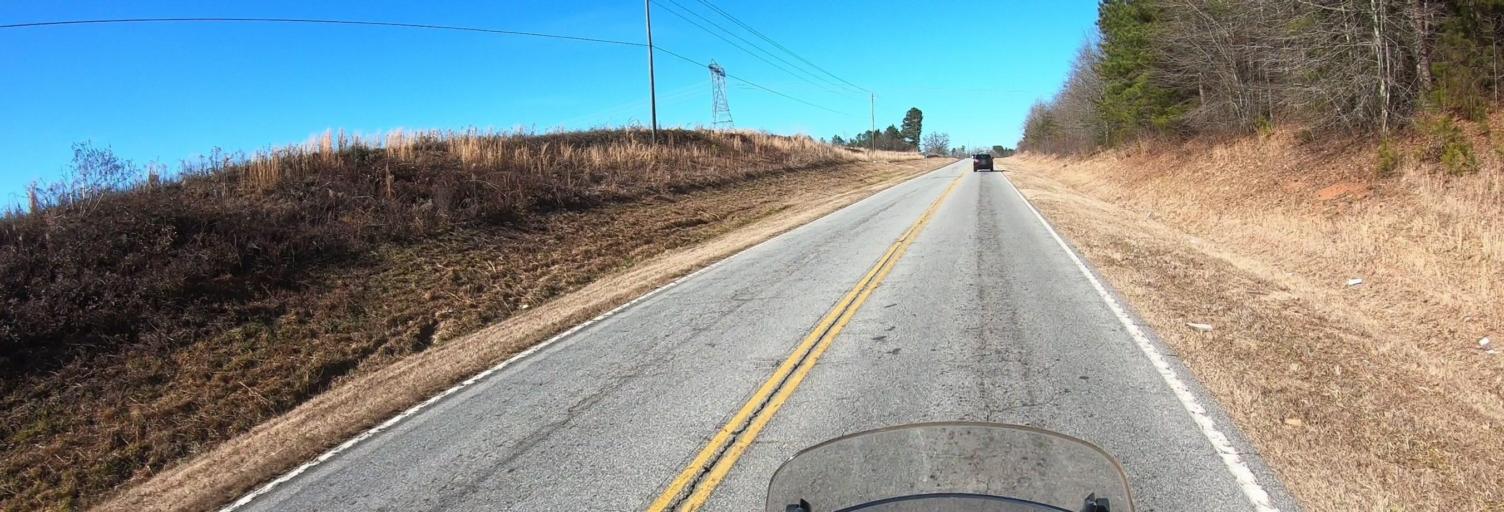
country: US
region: South Carolina
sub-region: Oconee County
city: Walhalla
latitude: 34.7288
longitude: -83.0616
